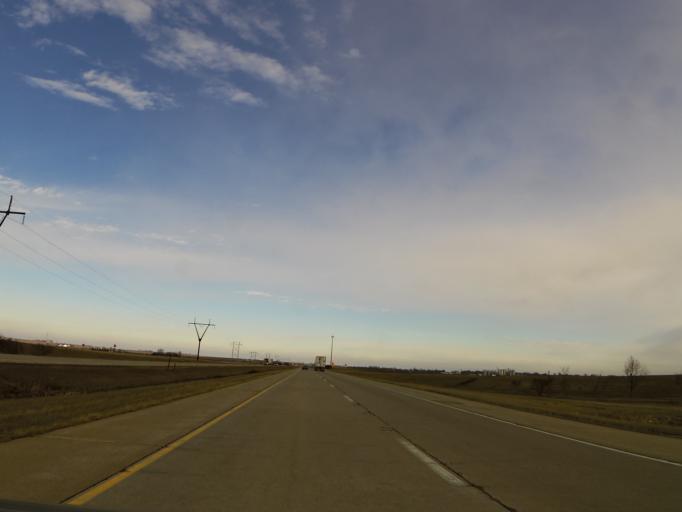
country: US
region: Illinois
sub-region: Marshall County
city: Wenona
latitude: 41.1194
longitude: -89.0753
